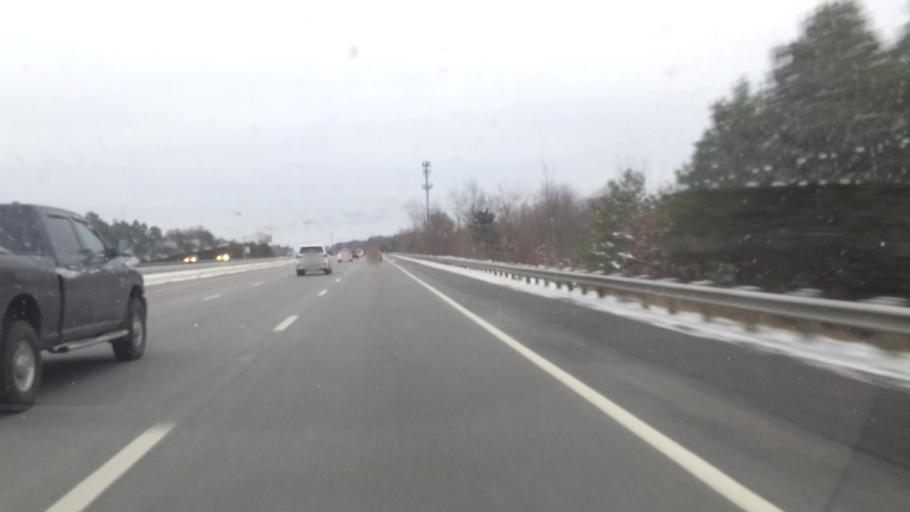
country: US
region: Ohio
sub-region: Cuyahoga County
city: Strongsville
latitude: 41.2946
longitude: -81.8086
